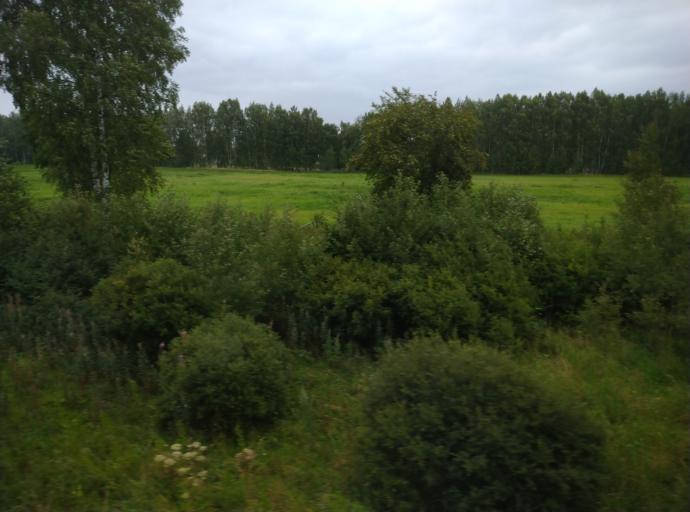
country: RU
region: Kostroma
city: Nerekhta
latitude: 57.4861
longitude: 40.5984
